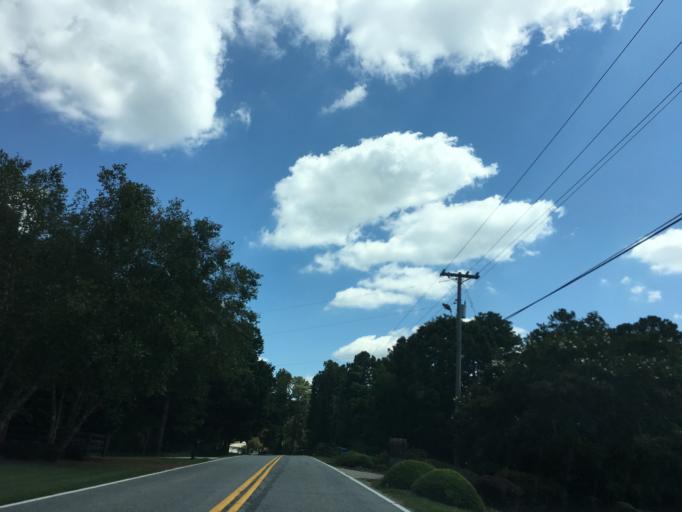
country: US
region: Georgia
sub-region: Fulton County
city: Milton
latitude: 34.1157
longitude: -84.2865
